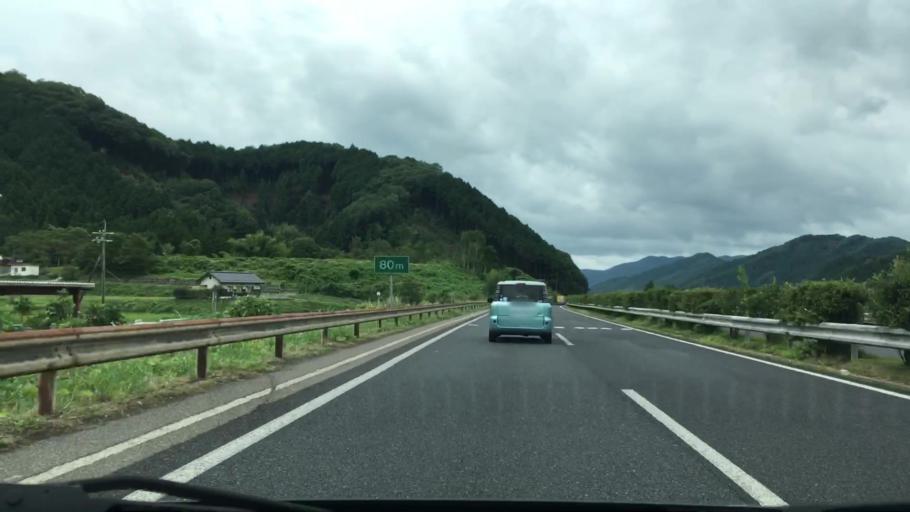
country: JP
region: Okayama
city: Tsuyama
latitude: 35.0339
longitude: 133.7862
